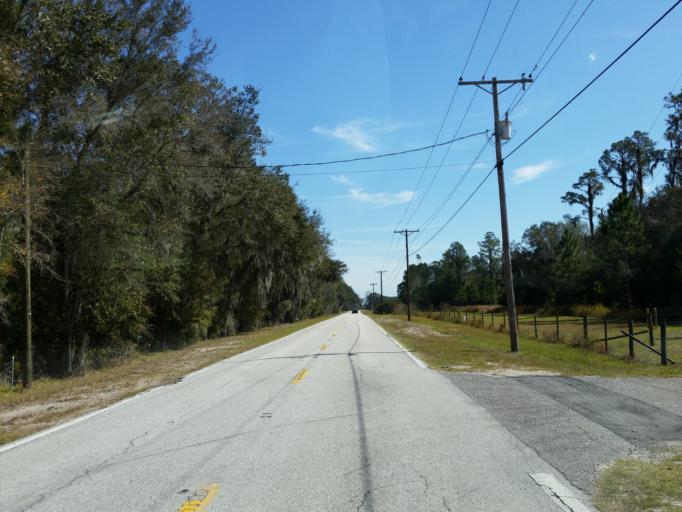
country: US
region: Florida
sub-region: Hillsborough County
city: Boyette
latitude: 27.8213
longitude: -82.2405
